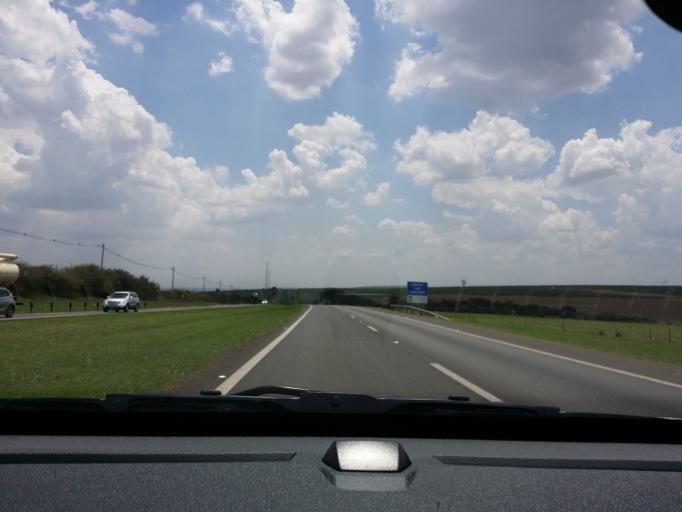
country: BR
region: Sao Paulo
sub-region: Itirapina
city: Itirapina
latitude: -22.2072
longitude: -47.7702
